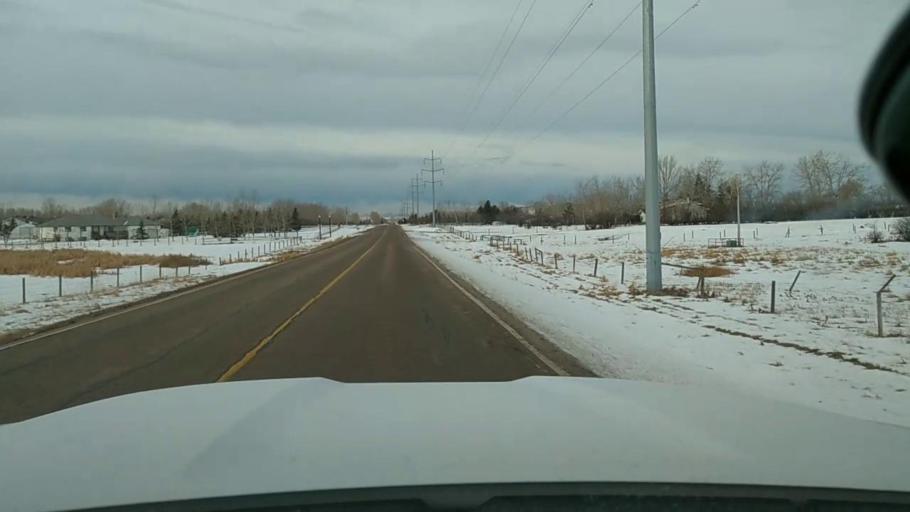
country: CA
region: Alberta
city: Airdrie
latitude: 51.2417
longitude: -113.9680
